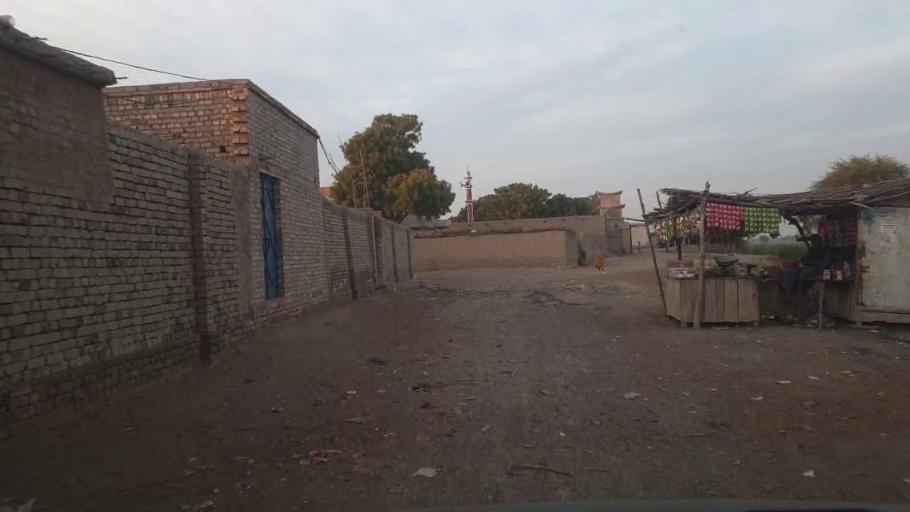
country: PK
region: Sindh
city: Shahpur Chakar
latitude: 26.0750
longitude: 68.5322
